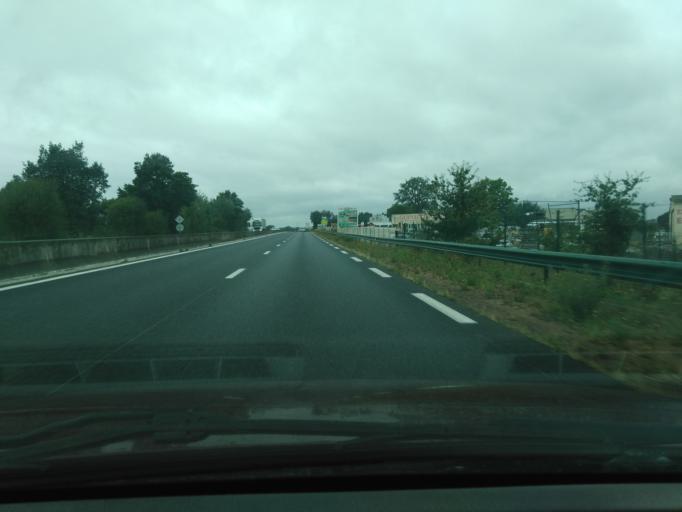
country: FR
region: Pays de la Loire
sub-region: Departement de la Vendee
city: La Chaize-le-Vicomte
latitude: 46.6678
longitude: -1.3354
